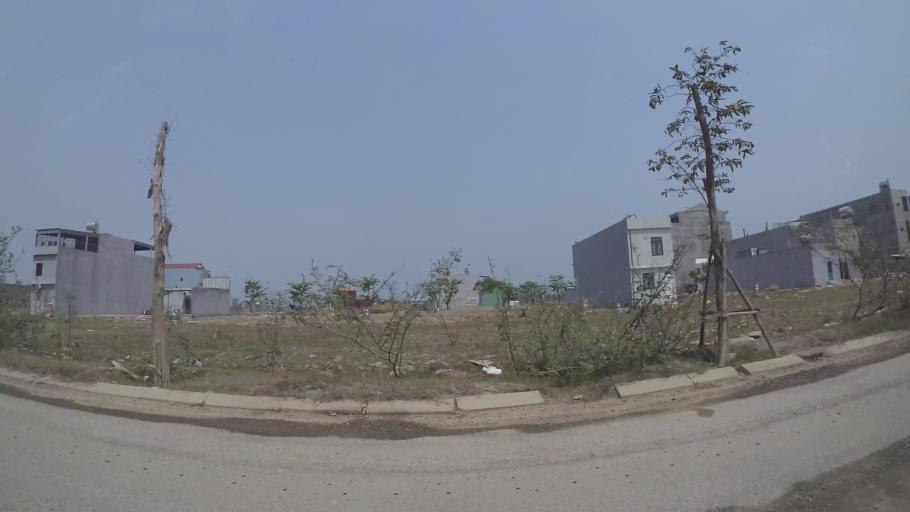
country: VN
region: Da Nang
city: Ngu Hanh Son
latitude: 16.0107
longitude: 108.2412
